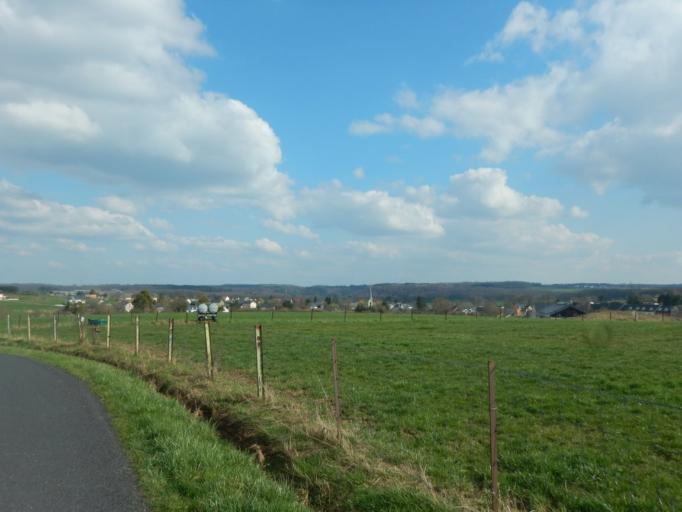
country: LU
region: Grevenmacher
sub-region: Canton d'Echternach
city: Waldbillig
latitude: 49.7995
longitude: 6.2751
